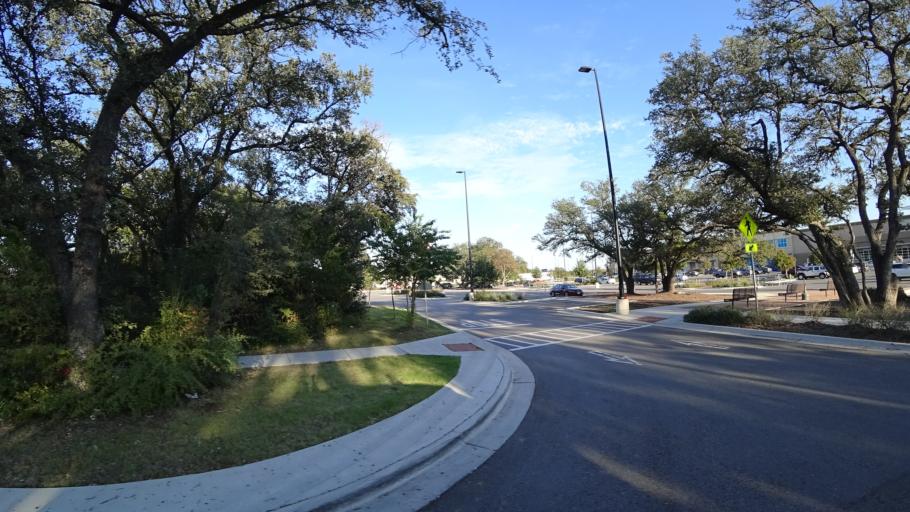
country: US
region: Texas
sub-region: Williamson County
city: Anderson Mill
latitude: 30.4738
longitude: -97.7963
